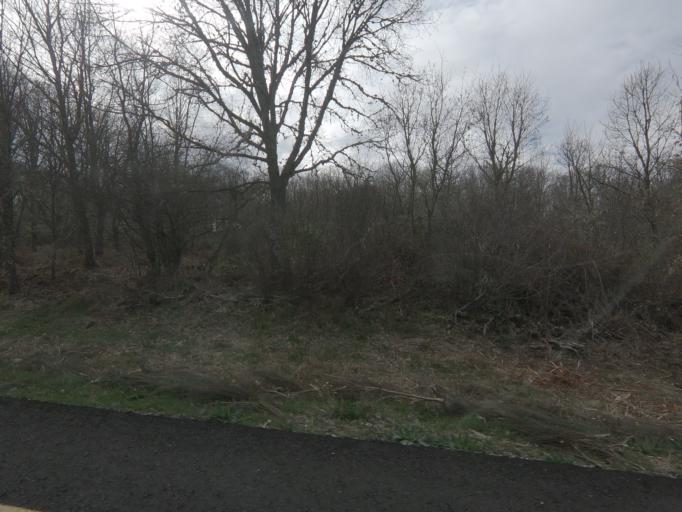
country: ES
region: Castille and Leon
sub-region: Provincia de Salamanca
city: Penaparda
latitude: 40.2799
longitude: -6.6770
